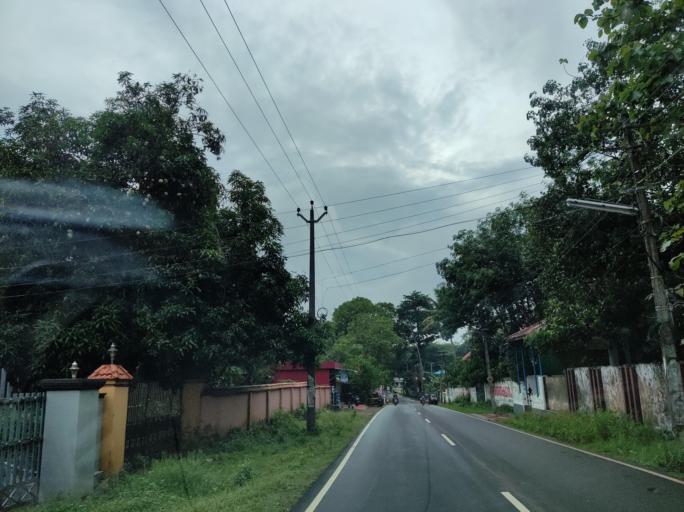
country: IN
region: Kerala
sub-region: Alappuzha
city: Mavelikara
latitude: 9.2304
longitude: 76.5678
